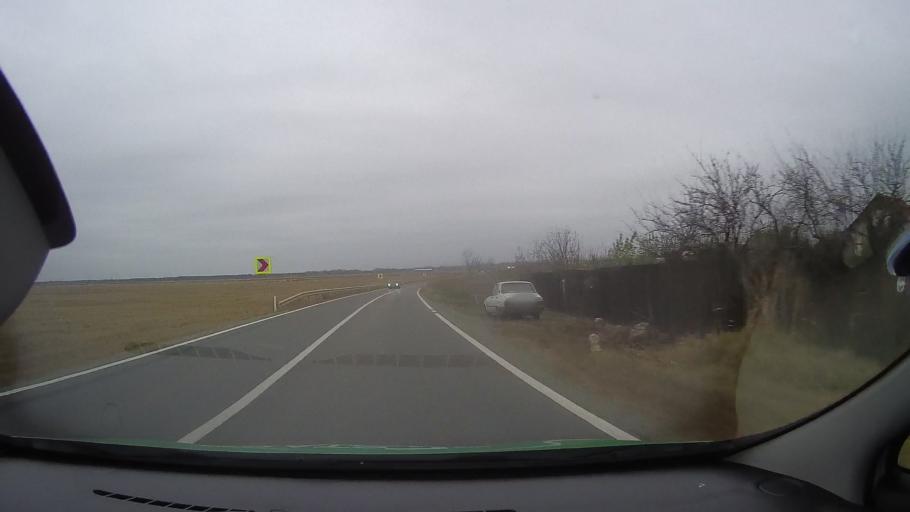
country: RO
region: Ialomita
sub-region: Comuna Slobozia
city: Slobozia
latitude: 44.5948
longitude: 27.3910
